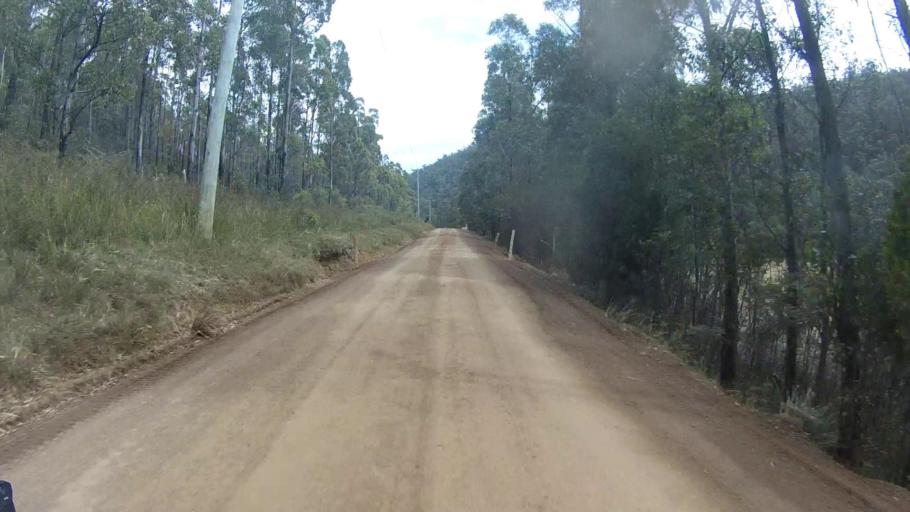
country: AU
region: Tasmania
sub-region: Sorell
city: Sorell
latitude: -42.7453
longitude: 147.7808
